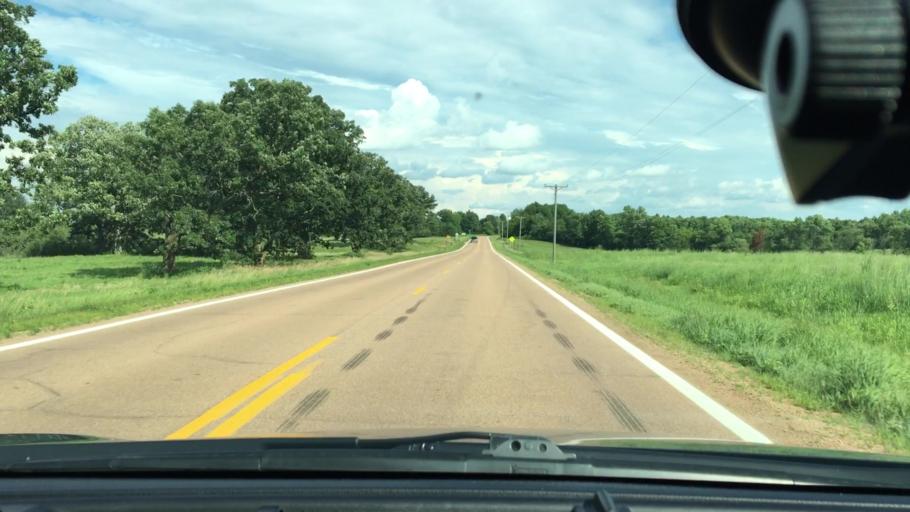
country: US
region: Minnesota
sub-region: Carver County
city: Victoria
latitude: 44.8795
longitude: -93.6987
